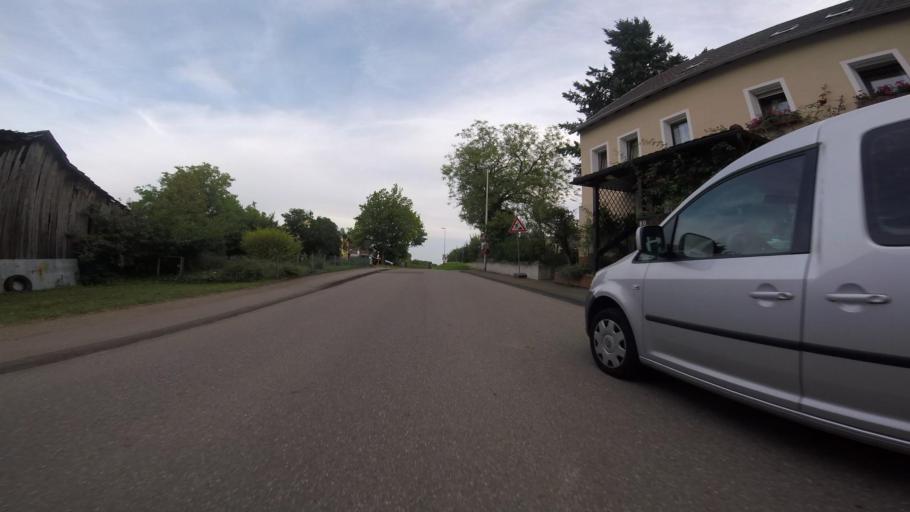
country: DE
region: Baden-Wuerttemberg
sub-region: Regierungsbezirk Stuttgart
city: Aspach
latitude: 48.9908
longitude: 9.3943
